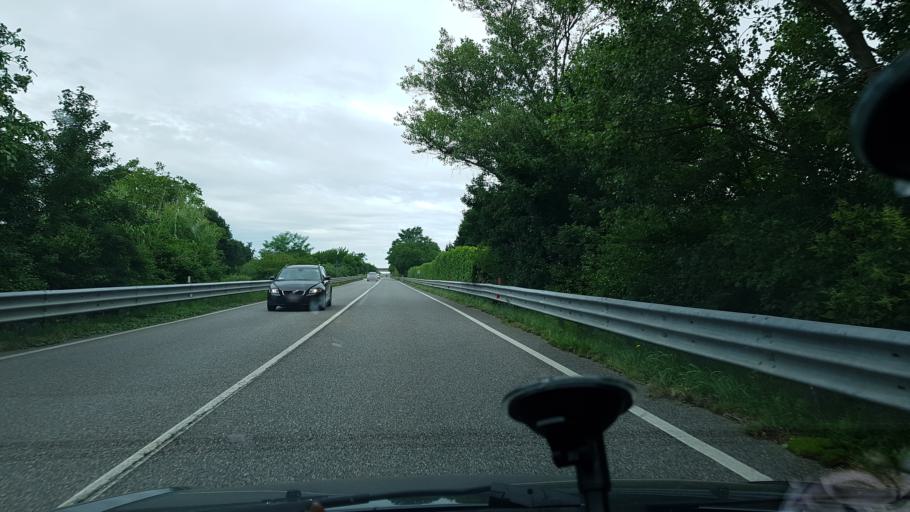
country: IT
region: Friuli Venezia Giulia
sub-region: Provincia di Gorizia
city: Savogna d'Isonzo
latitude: 45.9225
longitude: 13.5772
